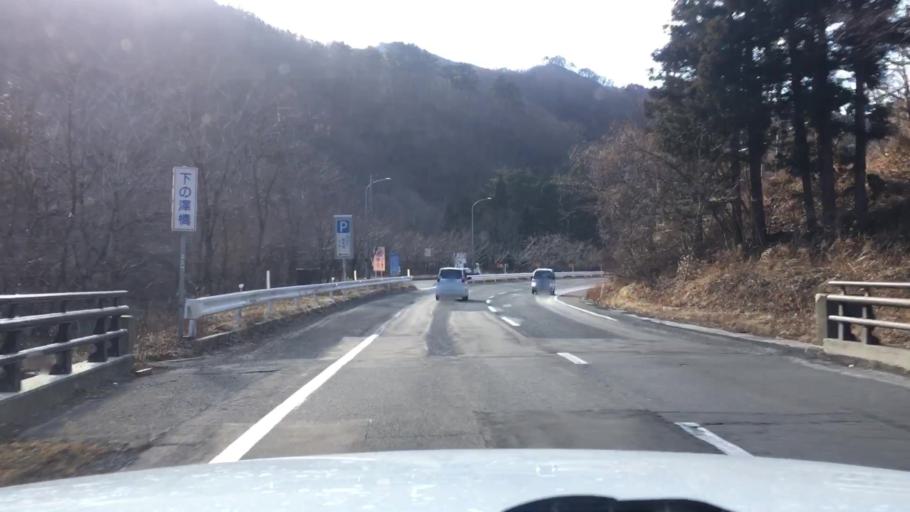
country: JP
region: Iwate
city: Miyako
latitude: 39.5965
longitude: 141.7214
